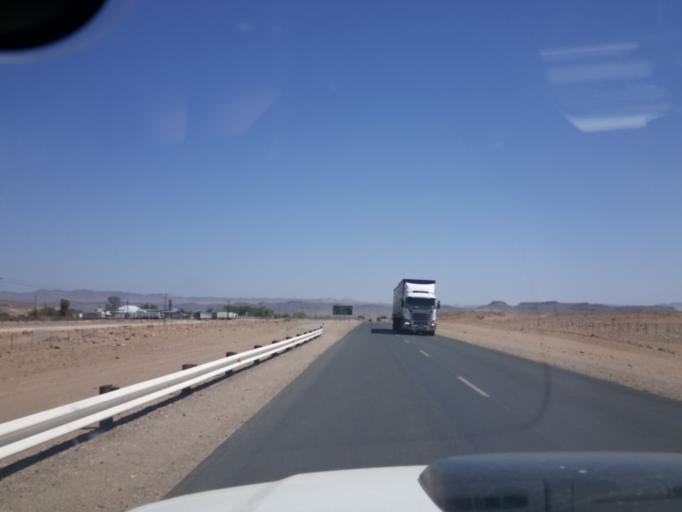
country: ZA
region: Northern Cape
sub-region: Namakwa District Municipality
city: Port Nolloth
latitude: -28.7404
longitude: 17.6175
